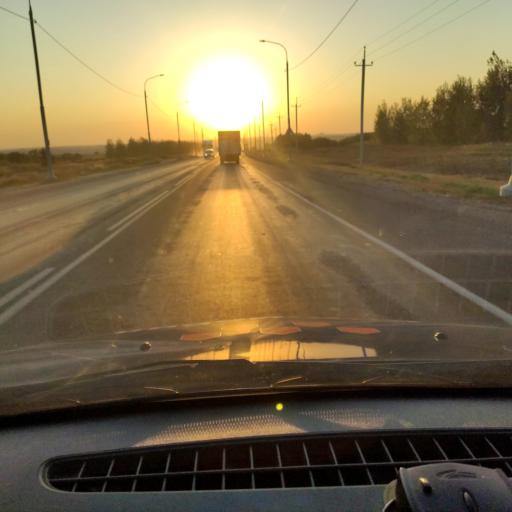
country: RU
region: Voronezj
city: Devitsa
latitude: 51.6310
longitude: 38.9746
